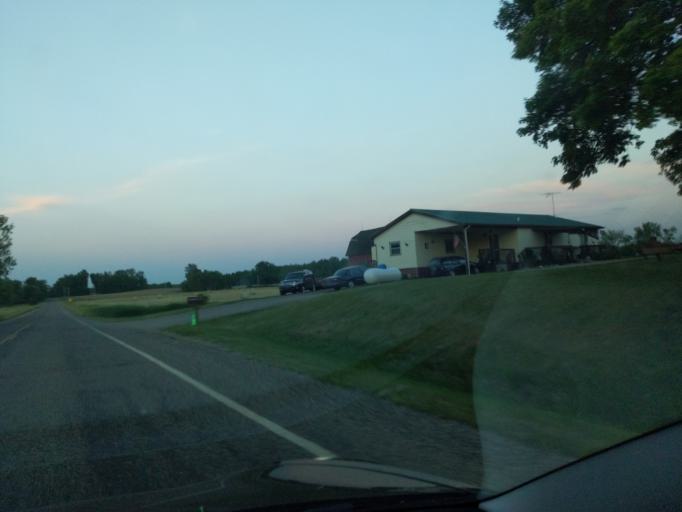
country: US
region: Michigan
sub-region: Barry County
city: Nashville
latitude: 42.5383
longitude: -85.0386
